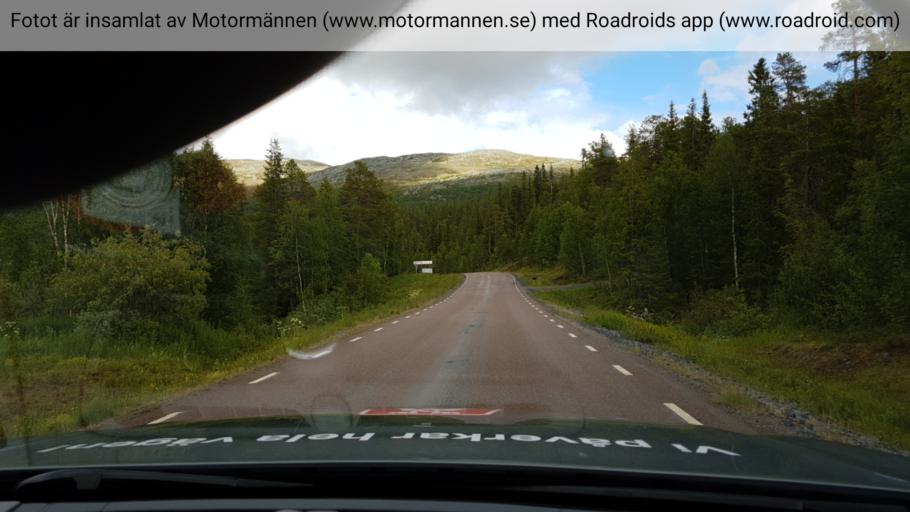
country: SE
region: Jaemtland
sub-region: Are Kommun
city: Jarpen
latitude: 63.0782
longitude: 13.7520
